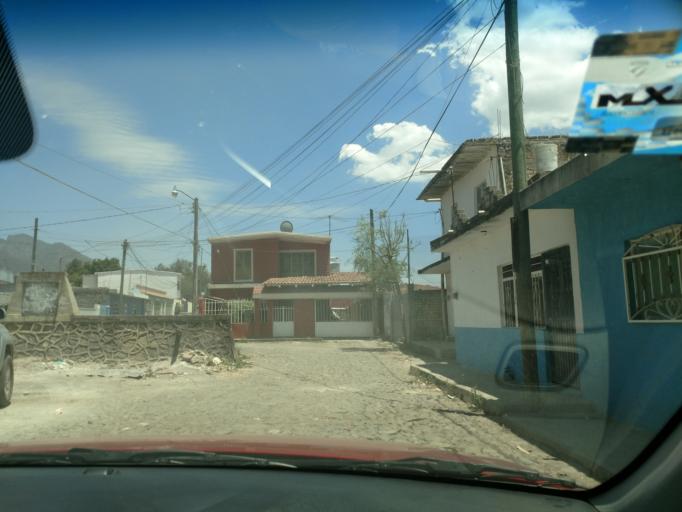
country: MX
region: Nayarit
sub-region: Tepic
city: La Corregidora
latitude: 21.4516
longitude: -104.8129
